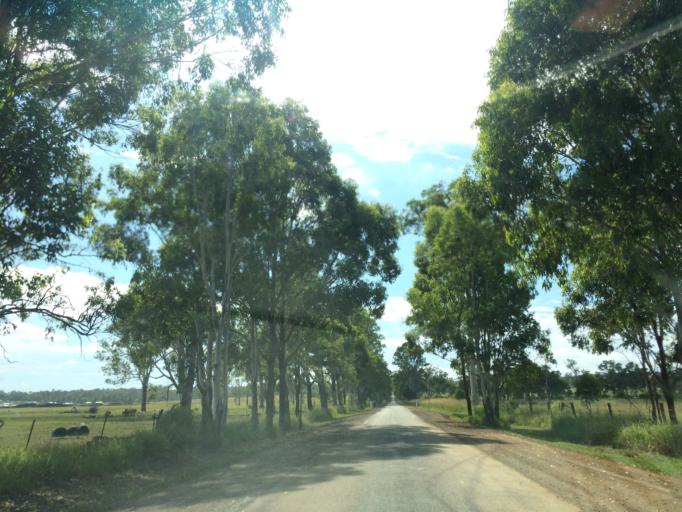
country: AU
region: Queensland
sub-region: Logan
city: Cedar Vale
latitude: -27.8797
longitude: 152.9564
